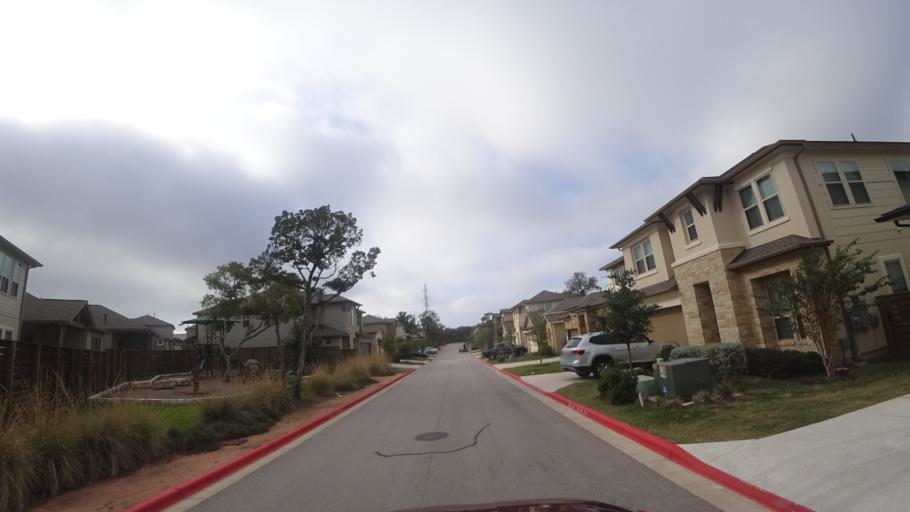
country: US
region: Texas
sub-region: Williamson County
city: Anderson Mill
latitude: 30.4008
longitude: -97.8429
